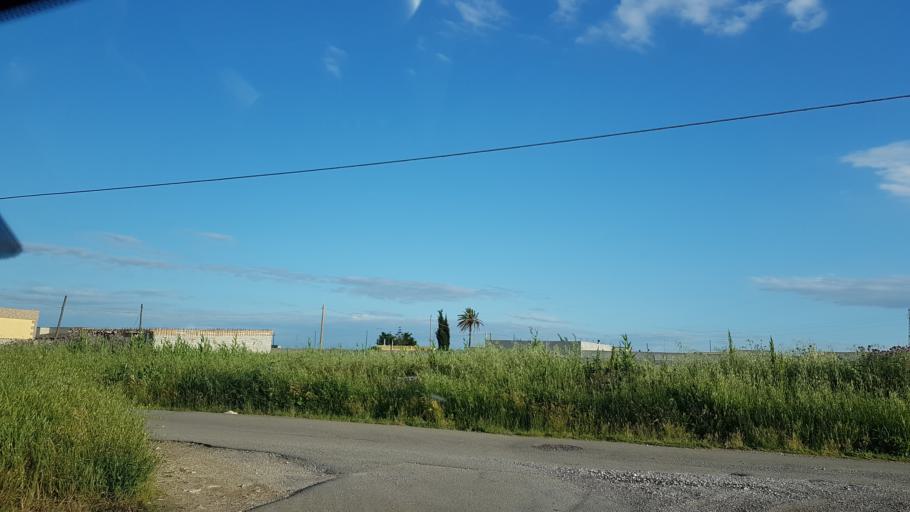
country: IT
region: Apulia
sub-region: Provincia di Brindisi
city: Brindisi
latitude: 40.6132
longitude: 17.9253
